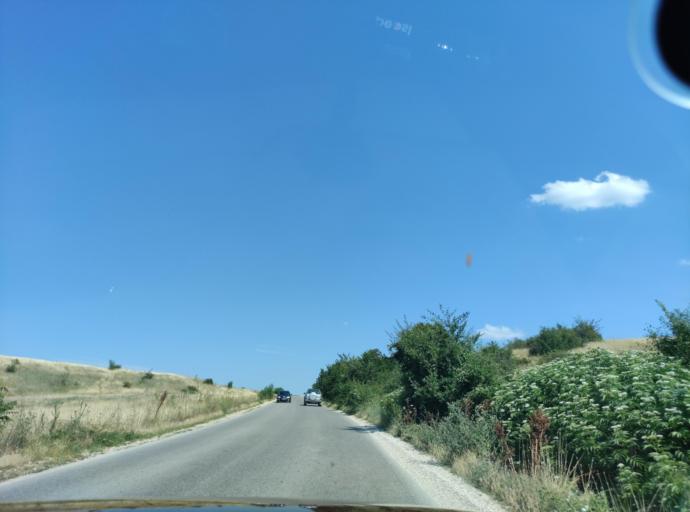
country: BG
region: Pleven
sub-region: Obshtina Cherven Bryag
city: Koynare
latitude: 43.3734
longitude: 24.0597
